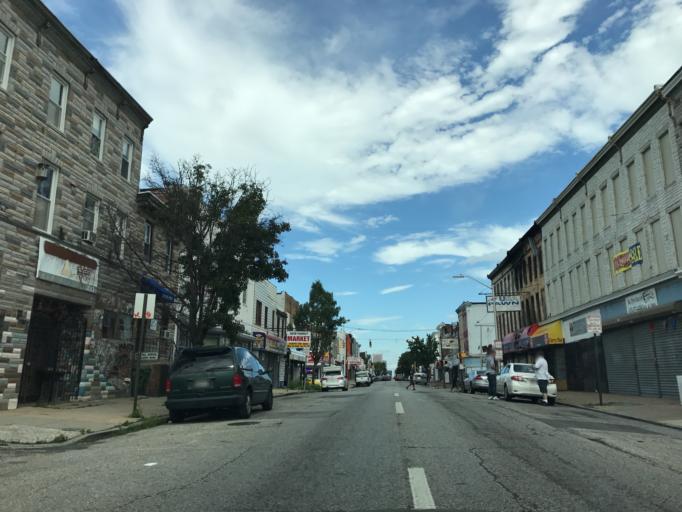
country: US
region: Maryland
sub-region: City of Baltimore
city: Baltimore
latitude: 39.2850
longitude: -76.6507
